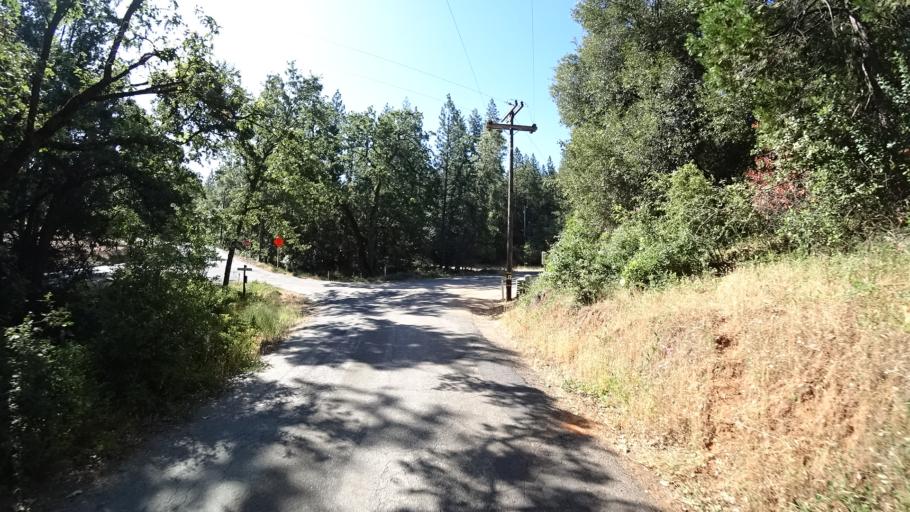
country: US
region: California
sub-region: Amador County
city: Pioneer
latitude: 38.4102
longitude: -120.5561
